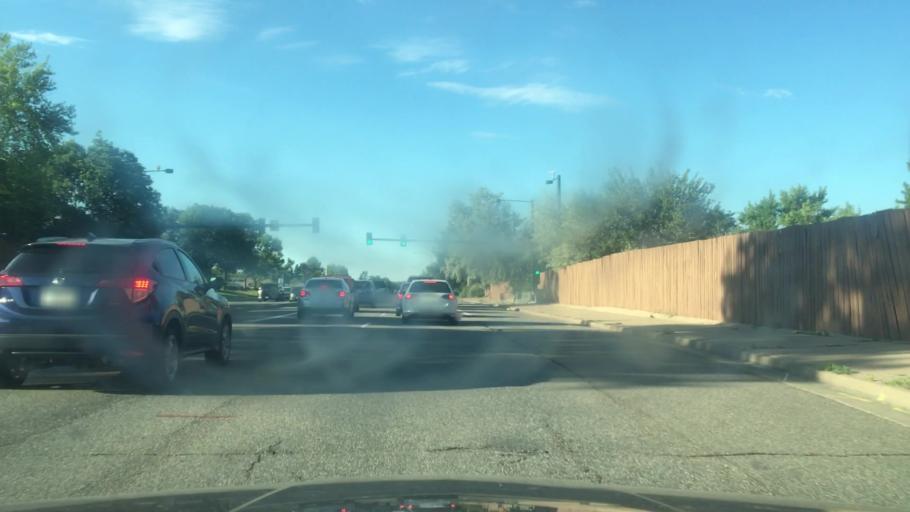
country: US
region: Colorado
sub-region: Arapahoe County
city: Castlewood
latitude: 39.6278
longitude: -104.8854
